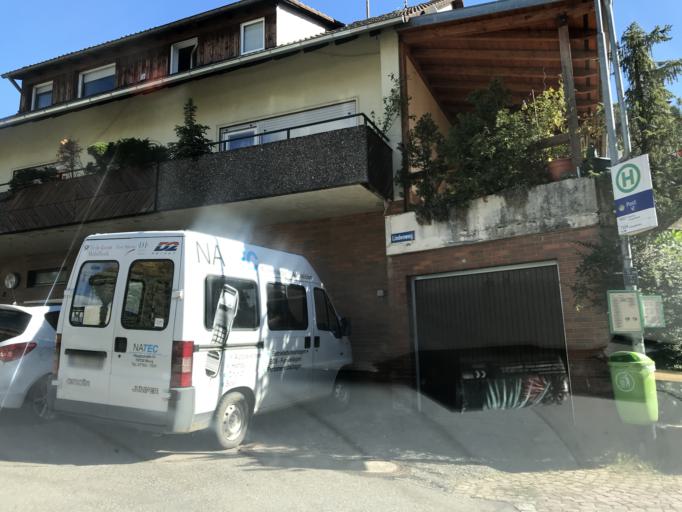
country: DE
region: Baden-Wuerttemberg
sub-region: Freiburg Region
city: Schopfheim
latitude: 47.6356
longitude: 7.8130
